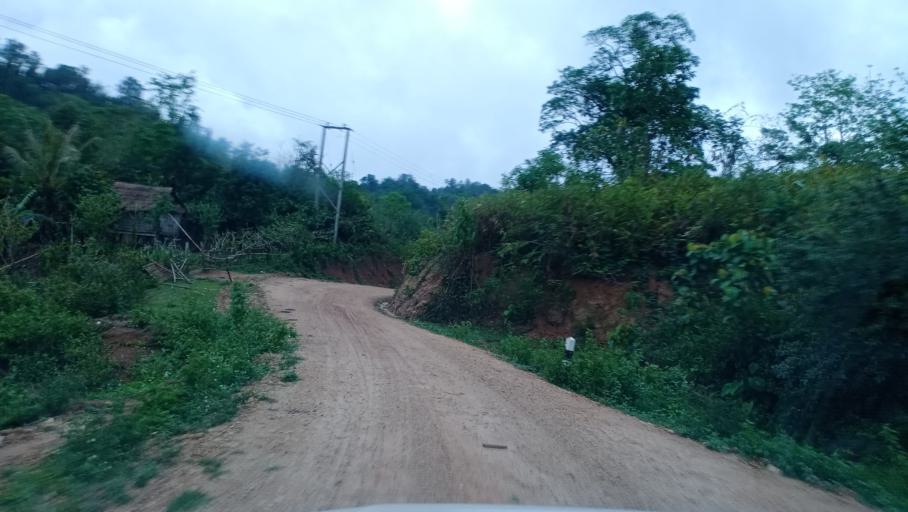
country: LA
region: Phongsali
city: Khoa
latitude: 21.2671
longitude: 102.7010
